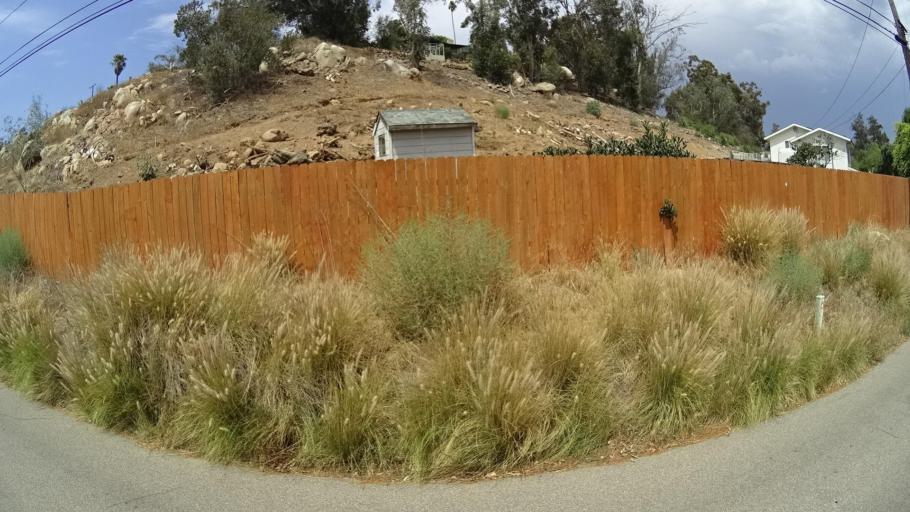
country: US
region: California
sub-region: San Diego County
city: Escondido
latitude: 33.1624
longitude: -117.1101
